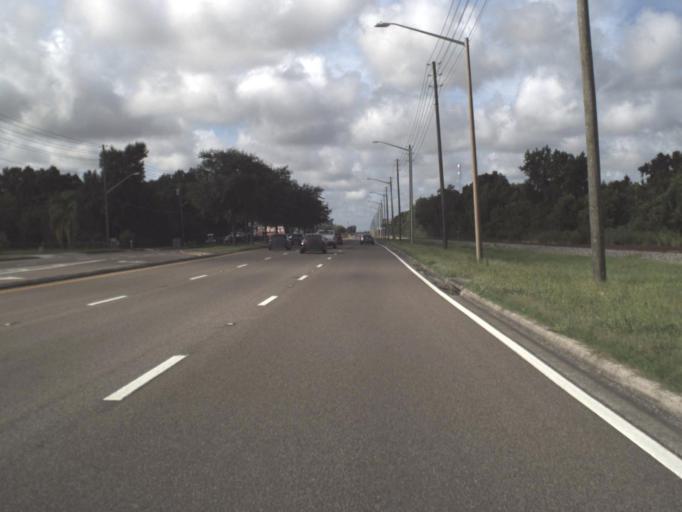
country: US
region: Florida
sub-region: Pasco County
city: Land O' Lakes
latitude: 28.2067
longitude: -82.4627
